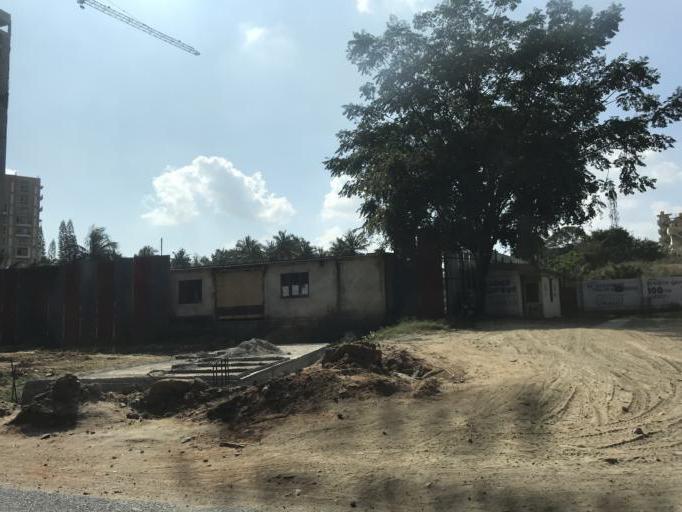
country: IN
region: Karnataka
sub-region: Bangalore Urban
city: Bangalore
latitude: 12.8440
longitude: 77.5881
